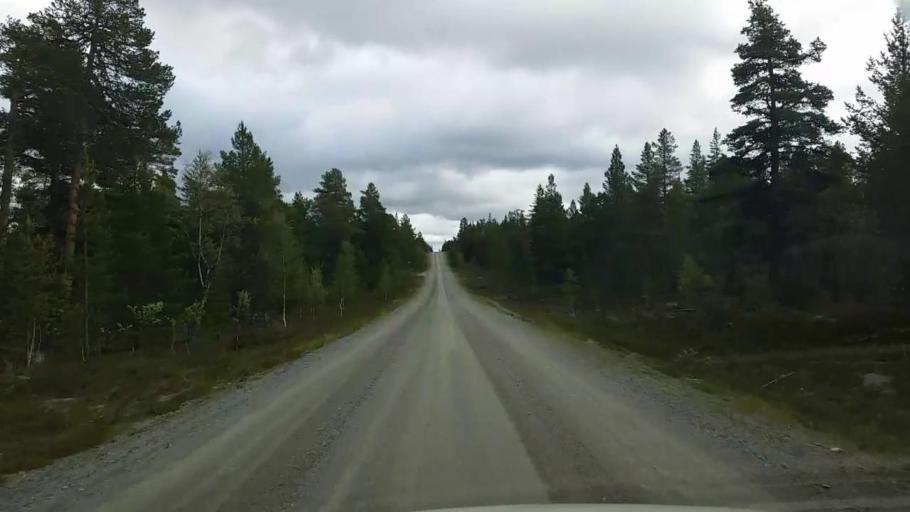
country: NO
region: Hedmark
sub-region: Engerdal
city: Engerdal
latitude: 62.3406
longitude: 12.6130
